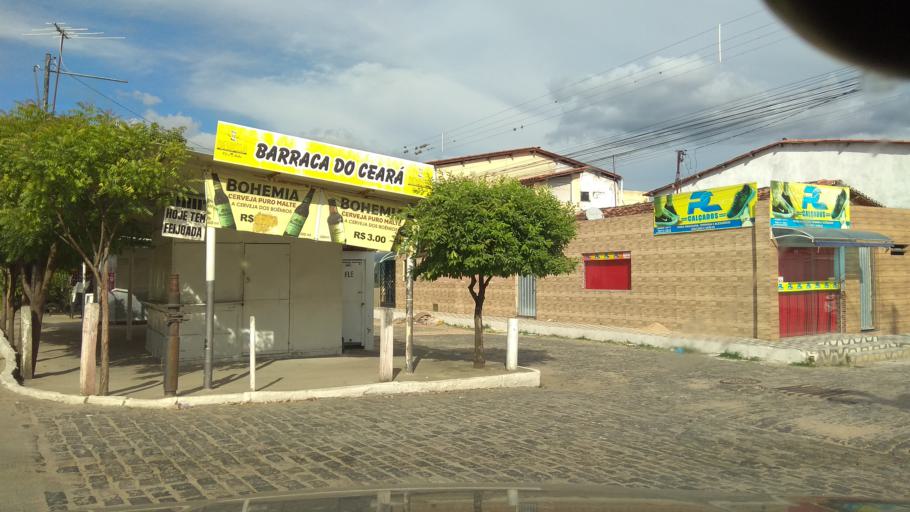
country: BR
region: Bahia
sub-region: Jequie
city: Jequie
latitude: -13.8718
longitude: -40.0688
